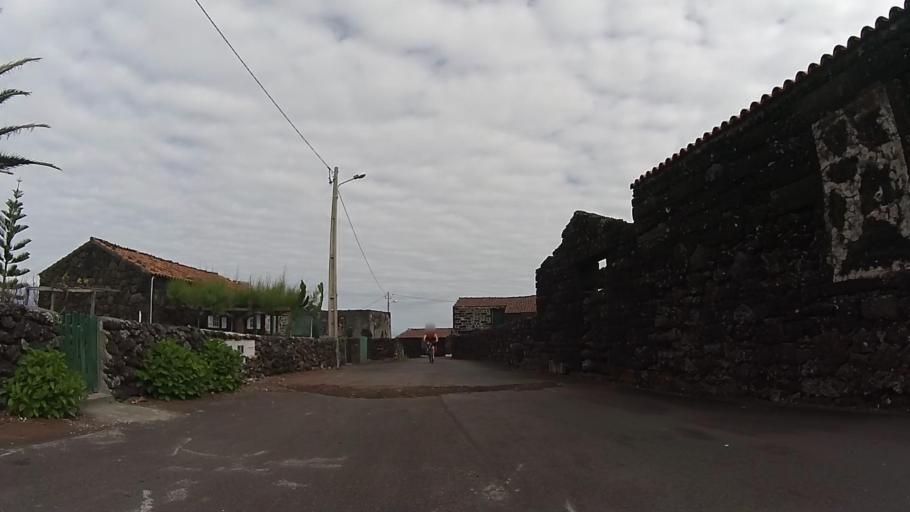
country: PT
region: Azores
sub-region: Madalena
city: Madalena
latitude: 38.5551
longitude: -28.4460
